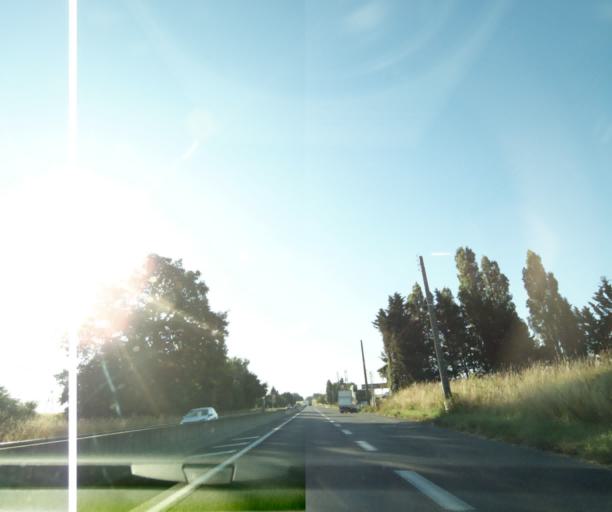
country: FR
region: Ile-de-France
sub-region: Departement de Seine-et-Marne
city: Vernou-la-Celle-sur-Seine
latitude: 48.3646
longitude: 2.8519
